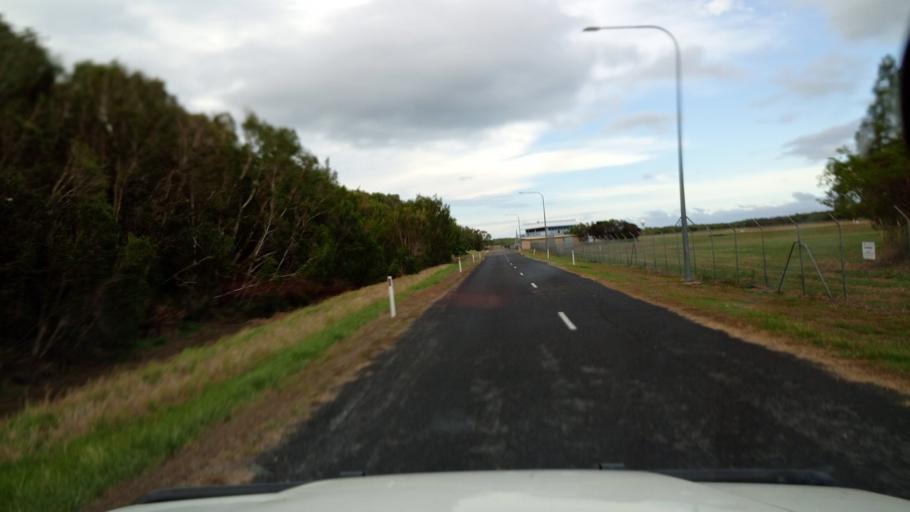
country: AU
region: Queensland
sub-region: Cairns
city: Redlynch
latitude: -16.8756
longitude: 145.7443
